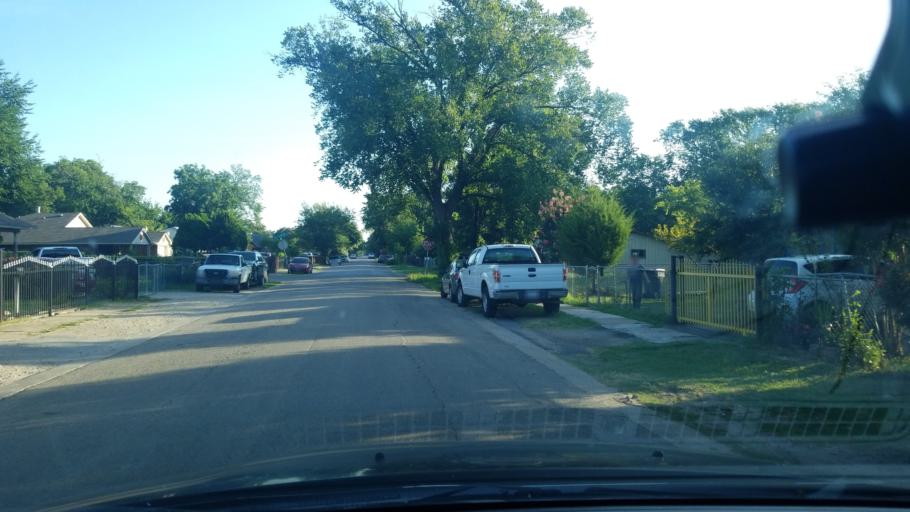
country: US
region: Texas
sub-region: Dallas County
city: Dallas
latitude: 32.7174
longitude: -96.8217
